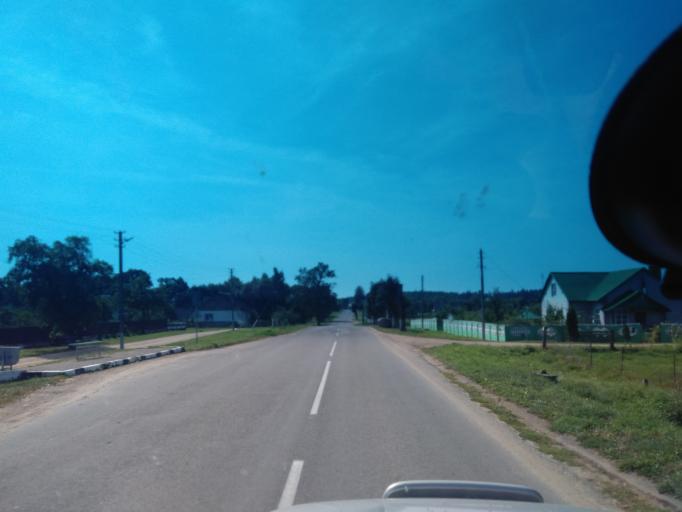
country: BY
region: Minsk
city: Kapyl'
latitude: 53.2065
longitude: 27.1210
